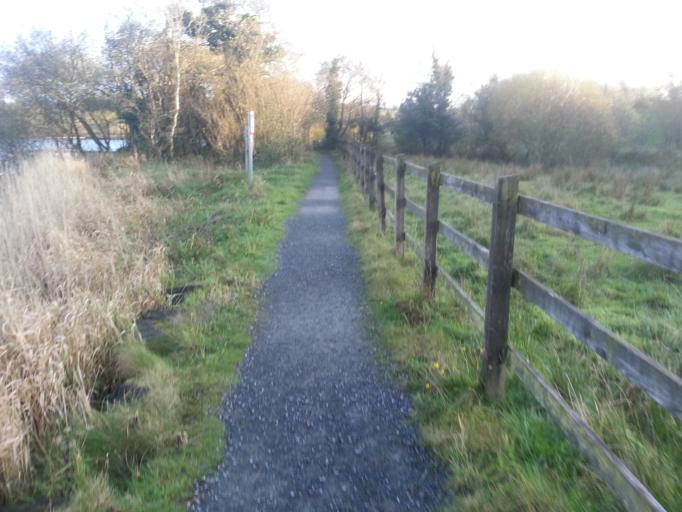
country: IE
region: Ulster
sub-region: County Monaghan
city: Clones
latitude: 54.2281
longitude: -7.2910
